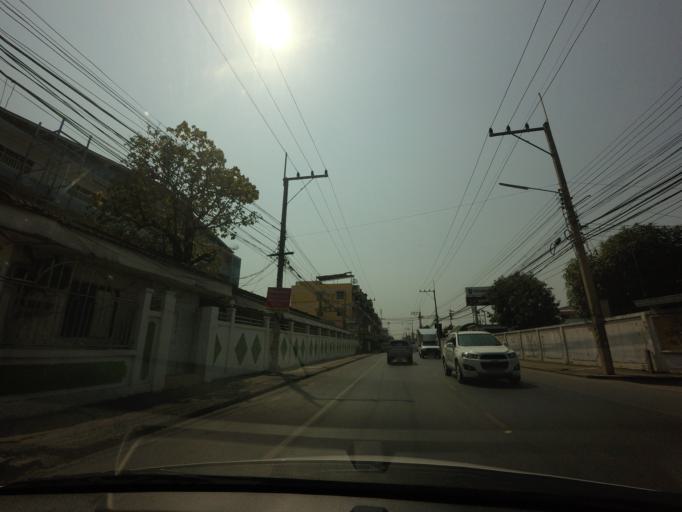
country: TH
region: Nakhon Pathom
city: Sam Phran
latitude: 13.7107
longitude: 100.2558
